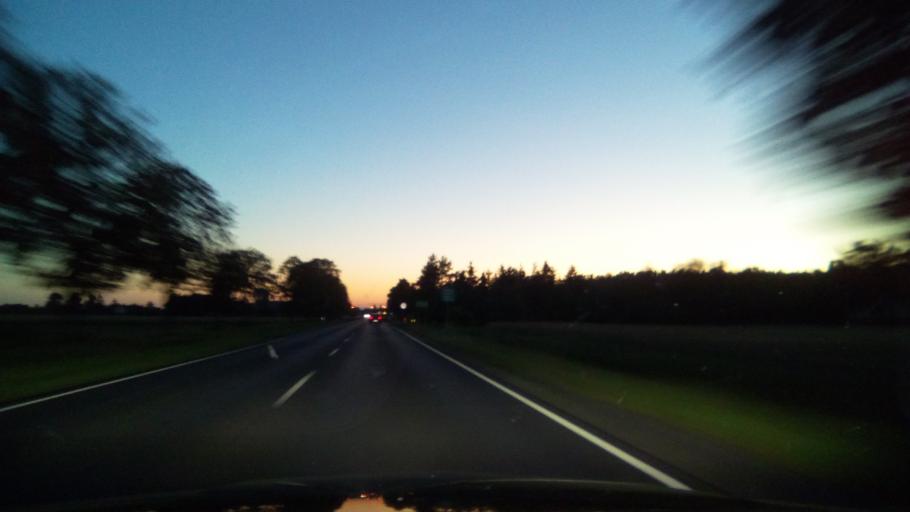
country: PL
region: Greater Poland Voivodeship
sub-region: Powiat koninski
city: Golina
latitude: 52.2478
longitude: 18.0259
